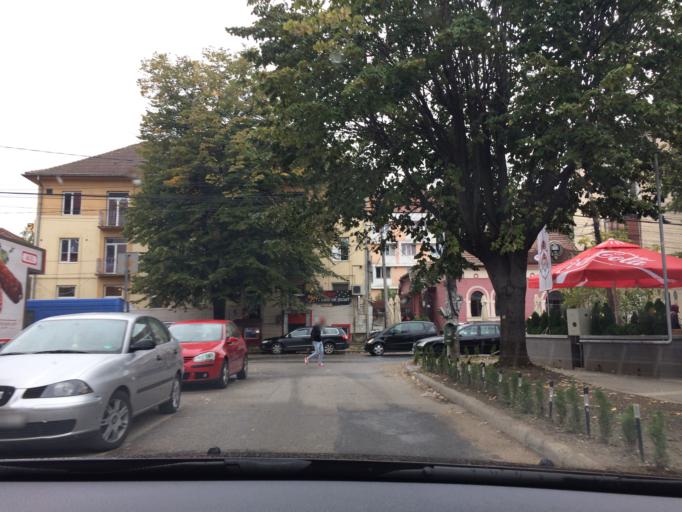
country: RO
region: Timis
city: Timisoara
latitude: 45.7505
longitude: 21.2429
